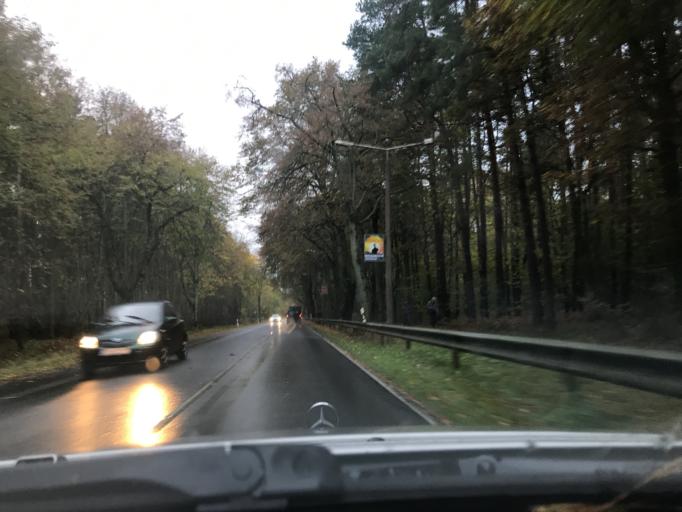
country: DE
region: Mecklenburg-Vorpommern
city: Seebad Heringsdorf
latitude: 53.9276
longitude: 14.2050
